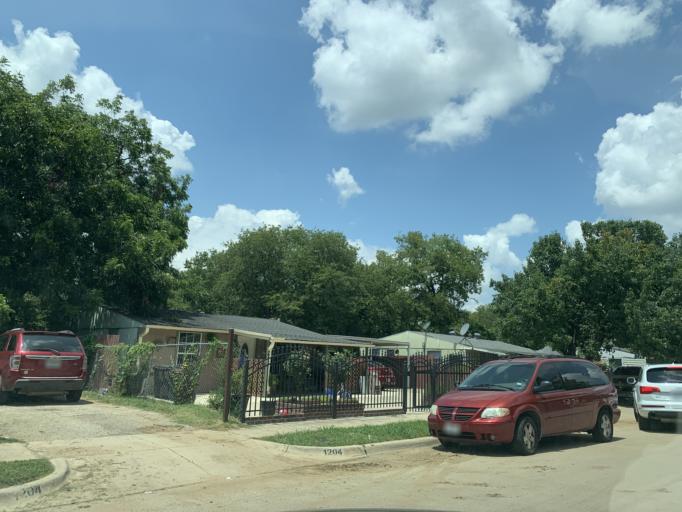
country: US
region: Texas
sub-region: Tarrant County
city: Fort Worth
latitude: 32.7322
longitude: -97.2633
